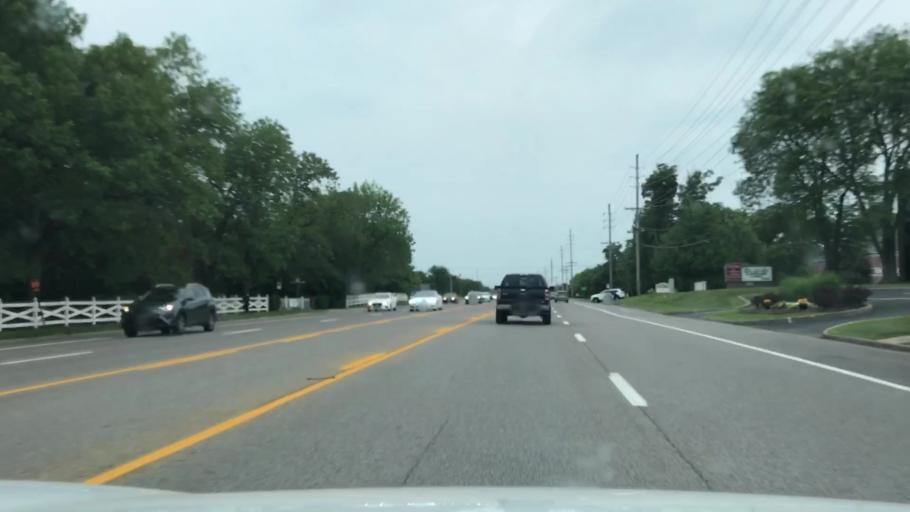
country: US
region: Missouri
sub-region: Saint Louis County
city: Clarkson Valley
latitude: 38.6096
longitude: -90.5857
